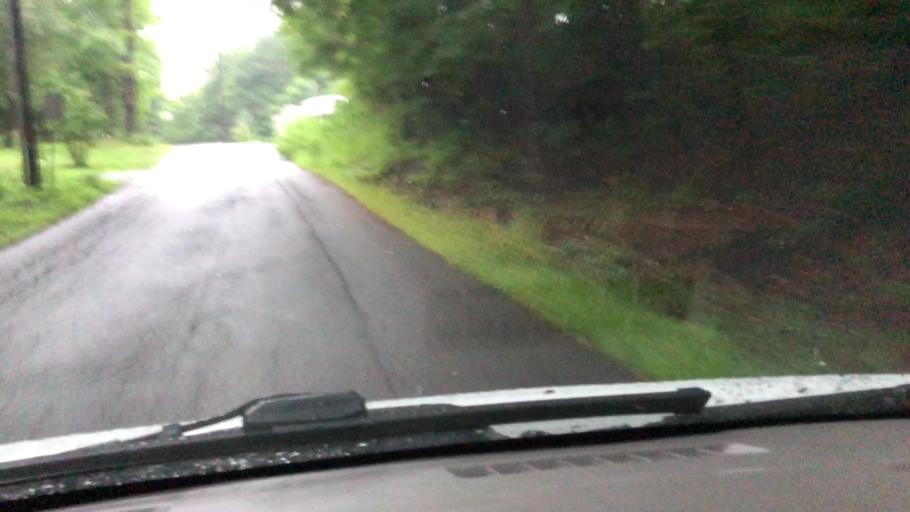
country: US
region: Massachusetts
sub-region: Hampshire County
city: Southampton
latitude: 42.2452
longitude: -72.7064
